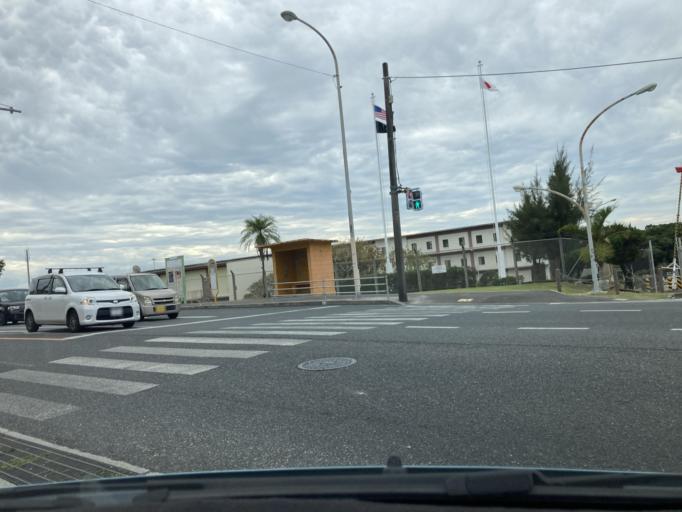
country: JP
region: Okinawa
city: Okinawa
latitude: 26.3854
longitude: 127.7395
